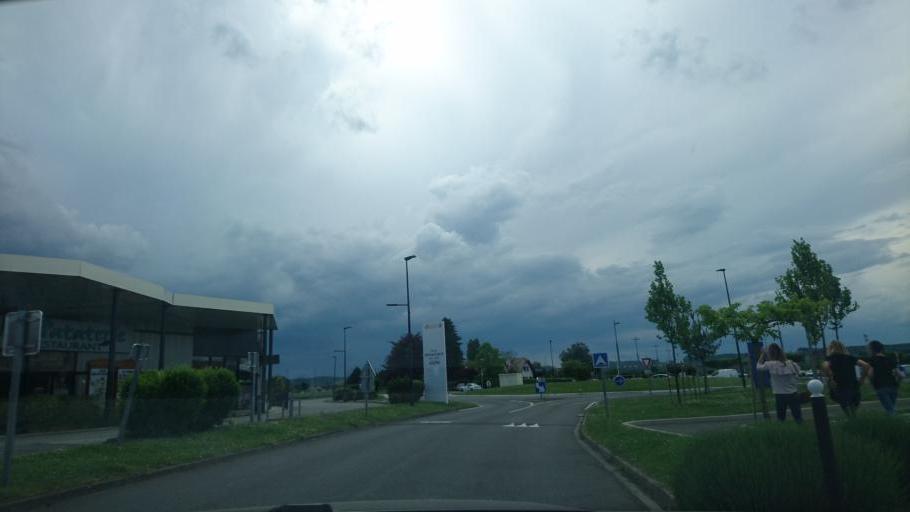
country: FR
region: Midi-Pyrenees
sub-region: Departement des Hautes-Pyrenees
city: Ibos
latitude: 43.2382
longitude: 0.0161
